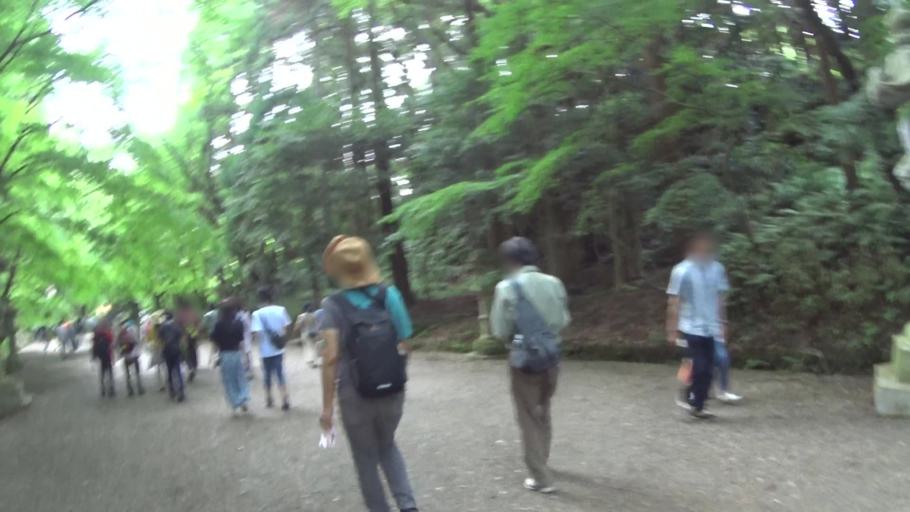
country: JP
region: Chiba
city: Sawara
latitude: 35.8844
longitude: 140.5283
